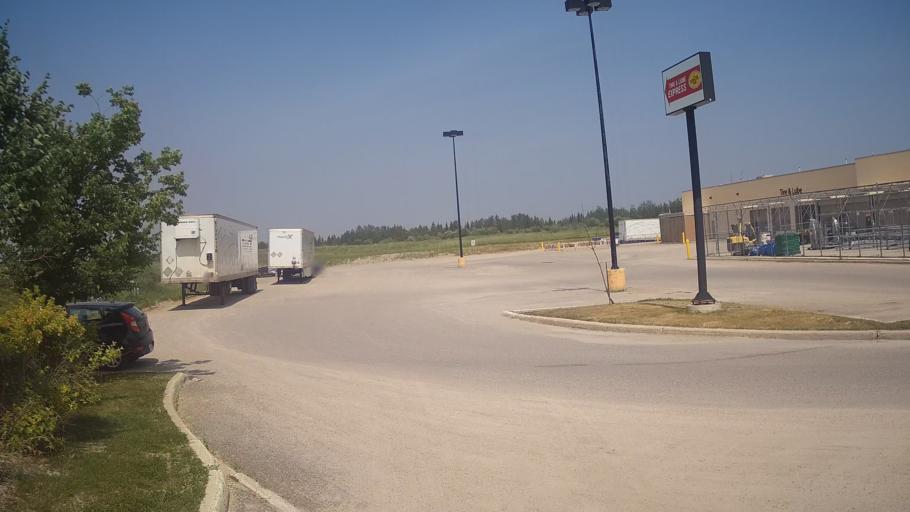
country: CA
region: Ontario
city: Timmins
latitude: 48.4744
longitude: -81.3952
